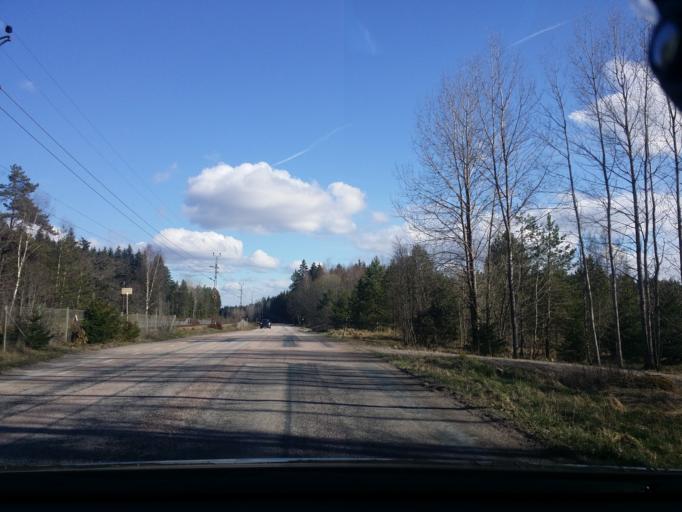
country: SE
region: Vaestmanland
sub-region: Sala Kommun
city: Sala
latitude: 59.9530
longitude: 16.5225
